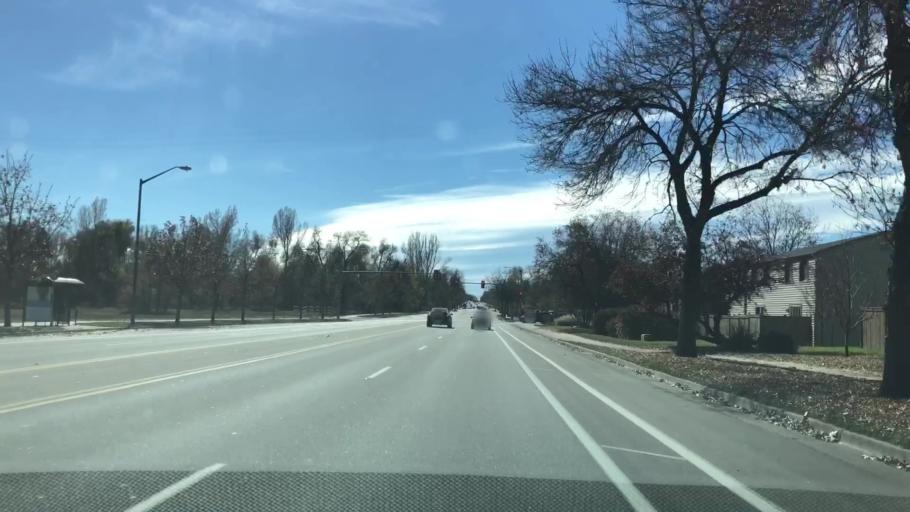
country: US
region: Colorado
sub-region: Larimer County
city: Fort Collins
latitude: 40.5648
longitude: -105.0960
